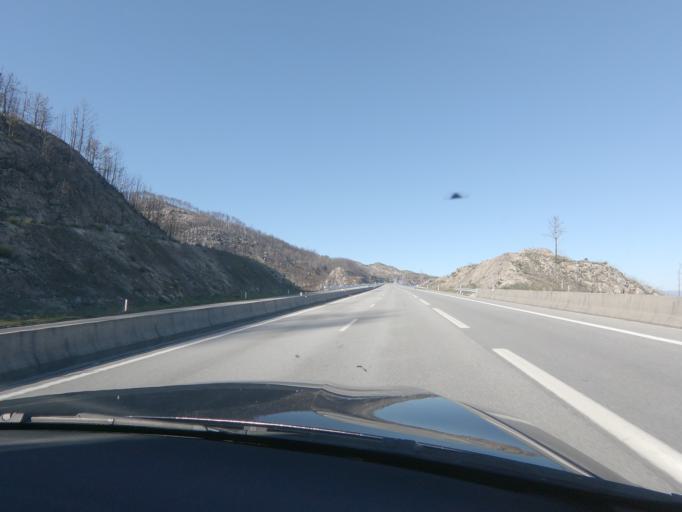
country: PT
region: Viseu
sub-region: Vouzela
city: Vouzela
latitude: 40.6681
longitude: -8.0749
